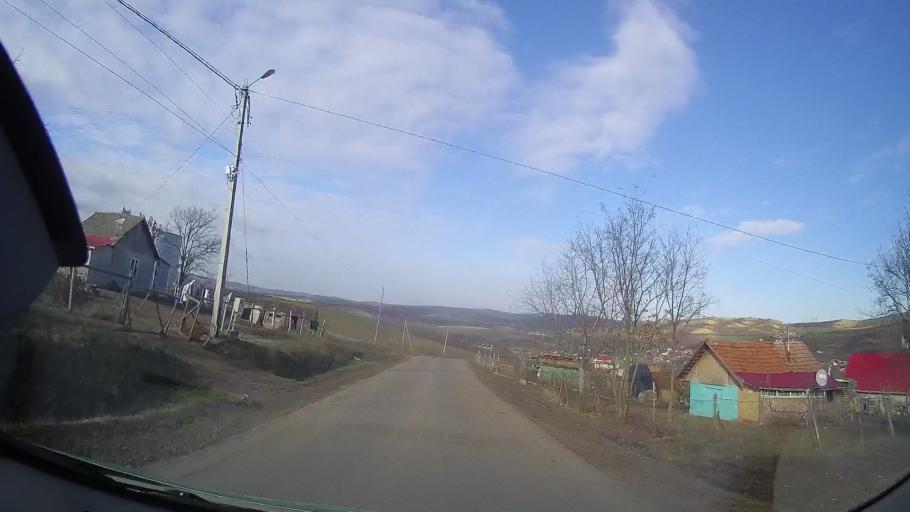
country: RO
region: Mures
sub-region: Comuna Sanger
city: Sanger
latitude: 46.5520
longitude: 24.1437
